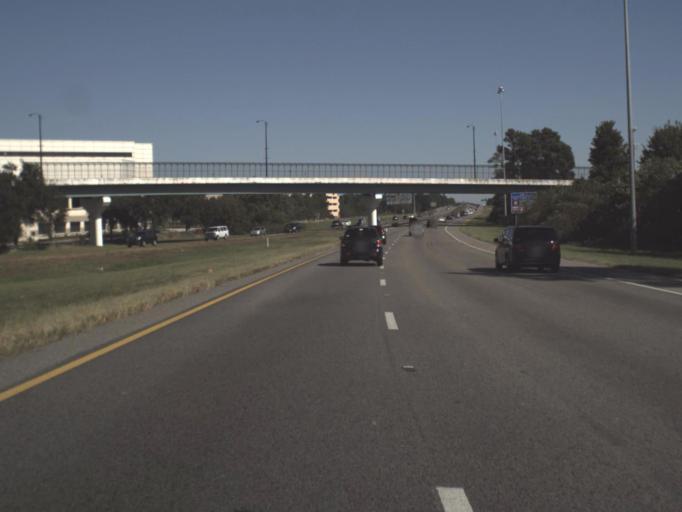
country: US
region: Florida
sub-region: Orange County
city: Williamsburg
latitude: 28.4207
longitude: -81.4696
